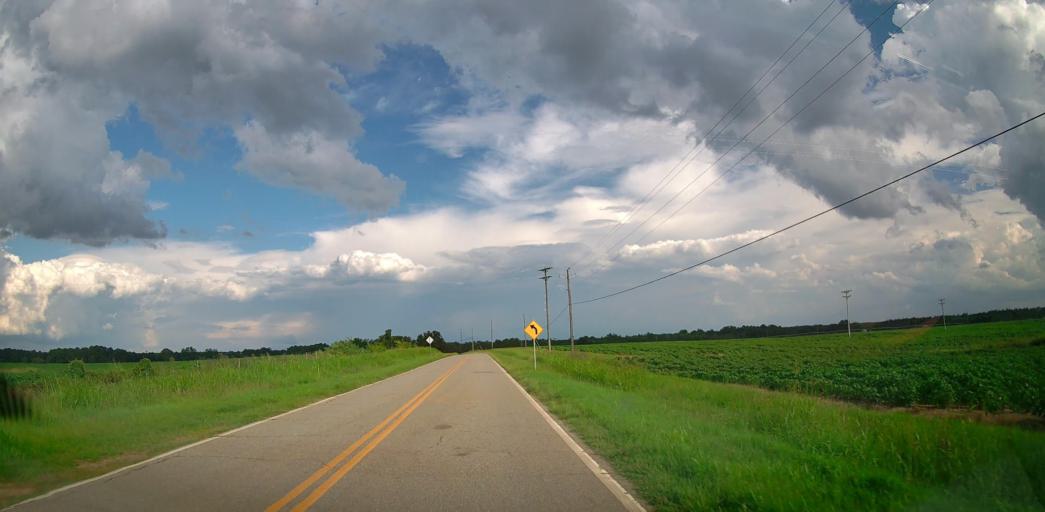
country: US
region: Georgia
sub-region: Bleckley County
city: Cochran
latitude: 32.3993
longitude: -83.3746
